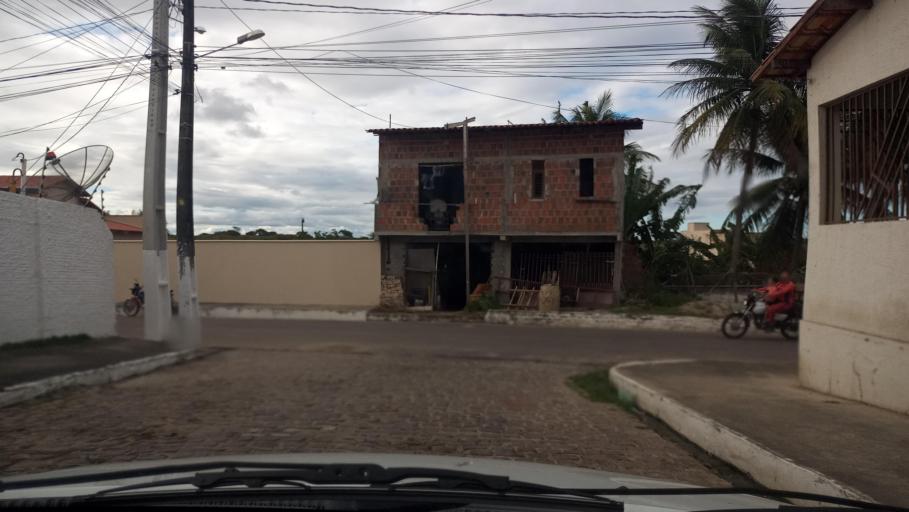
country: BR
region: Rio Grande do Norte
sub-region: Brejinho
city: Brejinho
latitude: -6.0444
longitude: -35.4321
